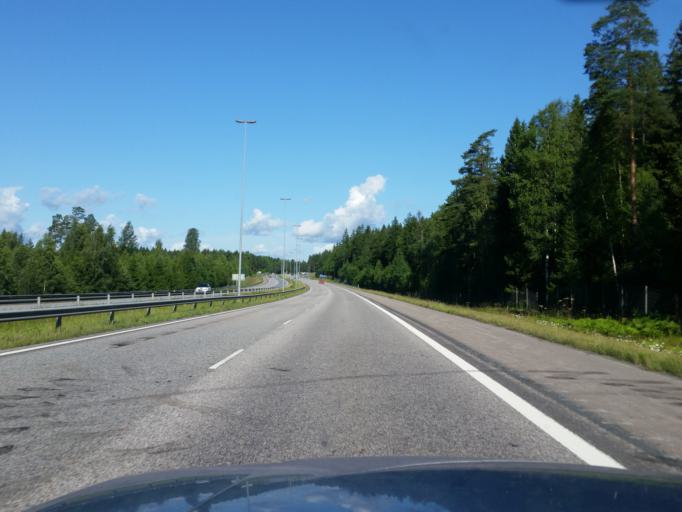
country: FI
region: Uusimaa
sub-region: Helsinki
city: Kirkkonummi
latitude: 60.2689
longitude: 24.4698
